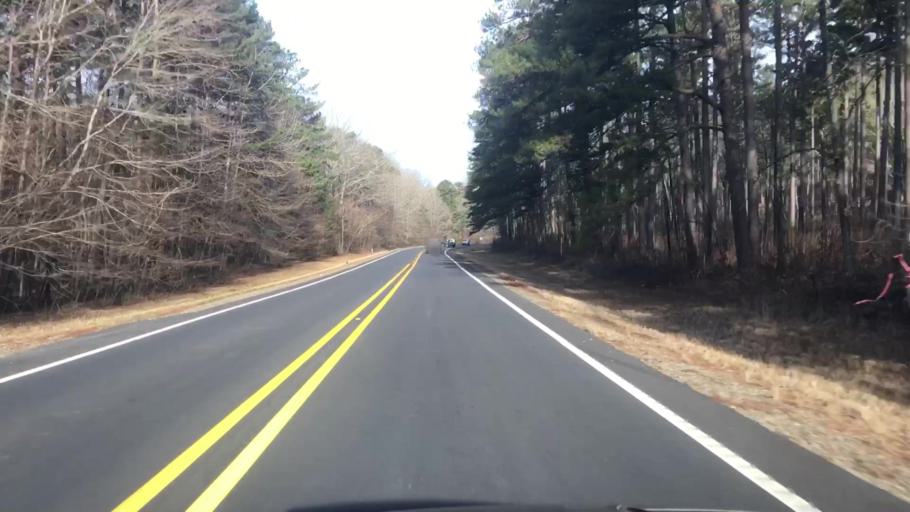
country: US
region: Arkansas
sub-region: Montgomery County
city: Mount Ida
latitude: 34.5183
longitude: -93.3869
